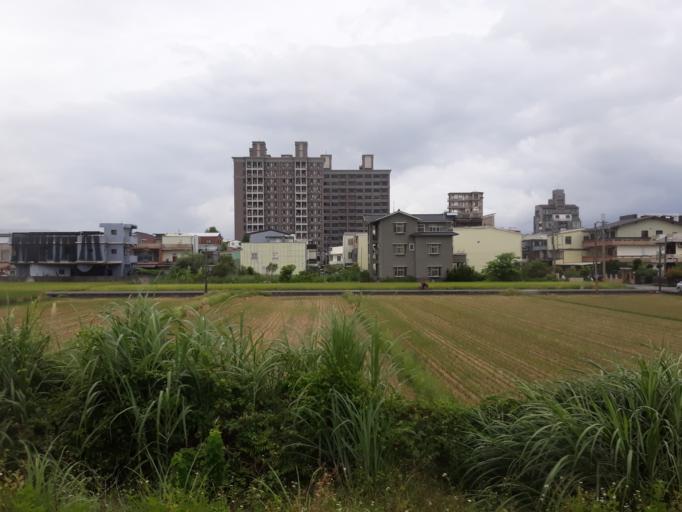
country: TW
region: Taiwan
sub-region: Yilan
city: Yilan
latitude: 24.6906
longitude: 121.7750
